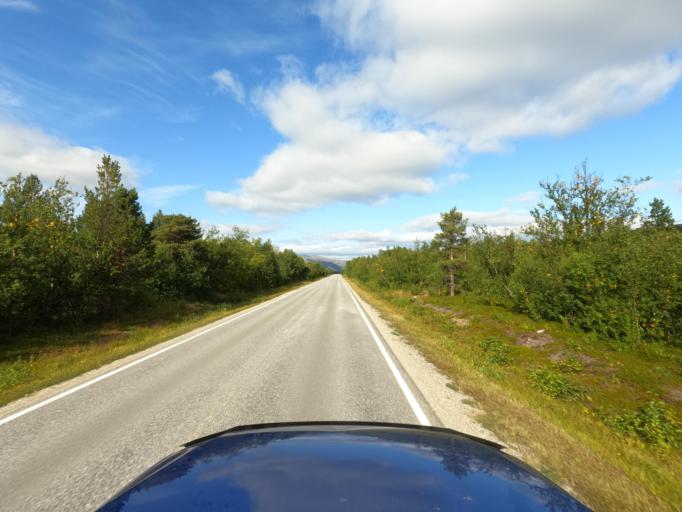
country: NO
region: Finnmark Fylke
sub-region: Porsanger
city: Lakselv
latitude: 69.9822
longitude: 24.9592
